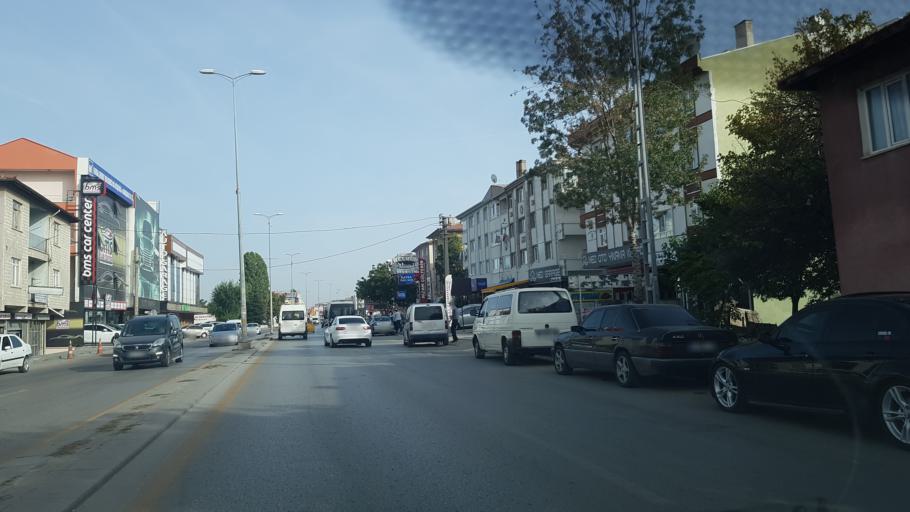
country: TR
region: Ankara
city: Etimesgut
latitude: 39.9519
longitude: 32.6462
